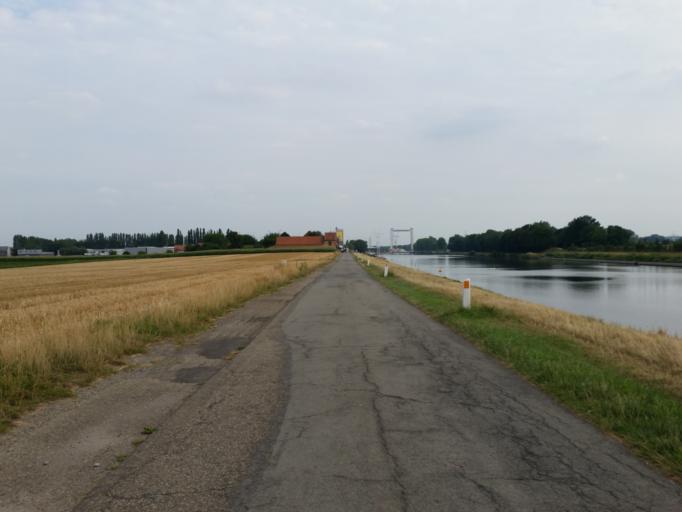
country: BE
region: Flanders
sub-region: Provincie Vlaams-Brabant
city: Vilvoorde
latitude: 50.9607
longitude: 4.4050
